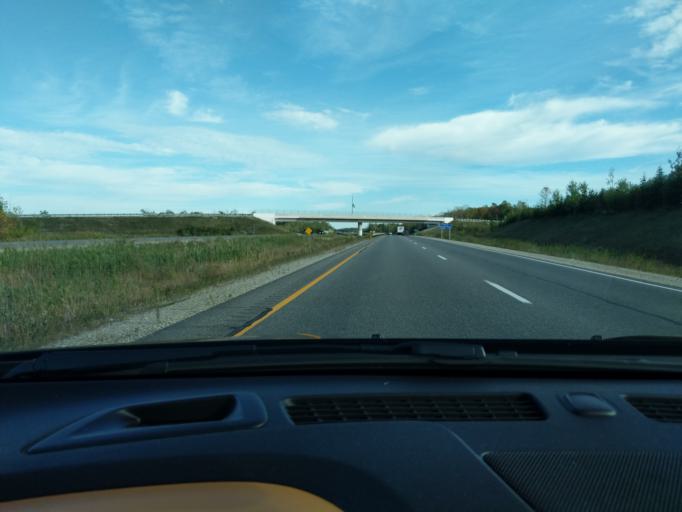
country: CA
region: Ontario
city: Collingwood
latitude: 44.4712
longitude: -80.1431
